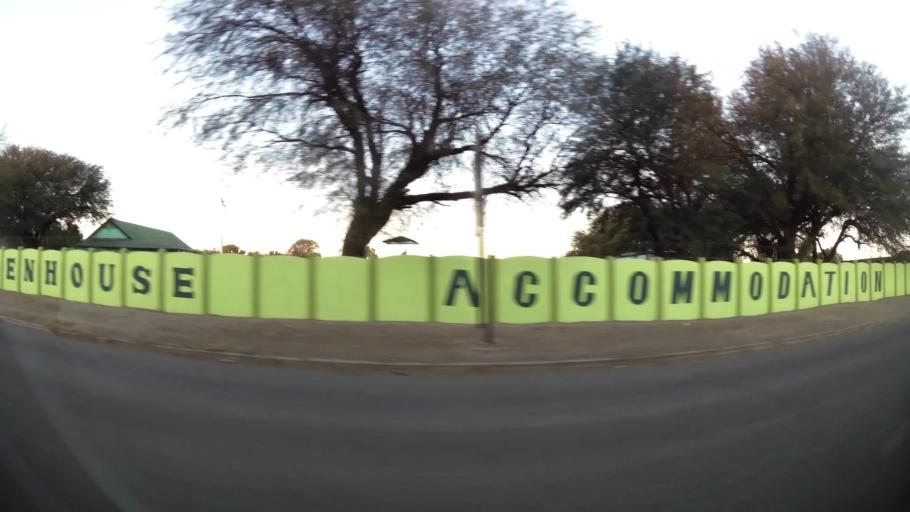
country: ZA
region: Northern Cape
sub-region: Frances Baard District Municipality
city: Kimberley
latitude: -28.7280
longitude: 24.7752
